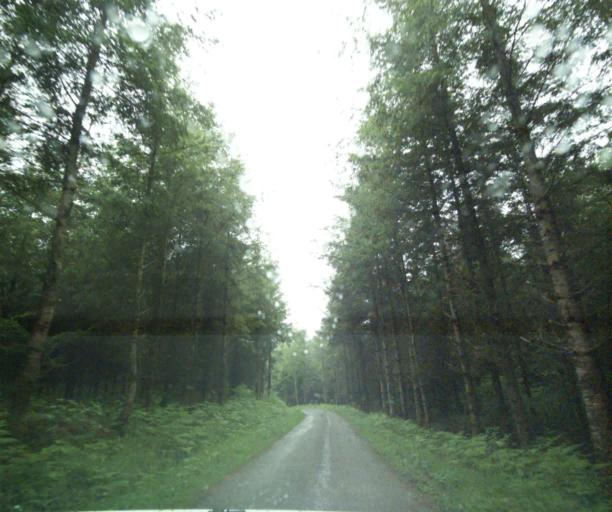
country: FR
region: Bourgogne
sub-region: Departement de Saone-et-Loire
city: La Clayette
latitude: 46.3716
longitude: 4.3659
